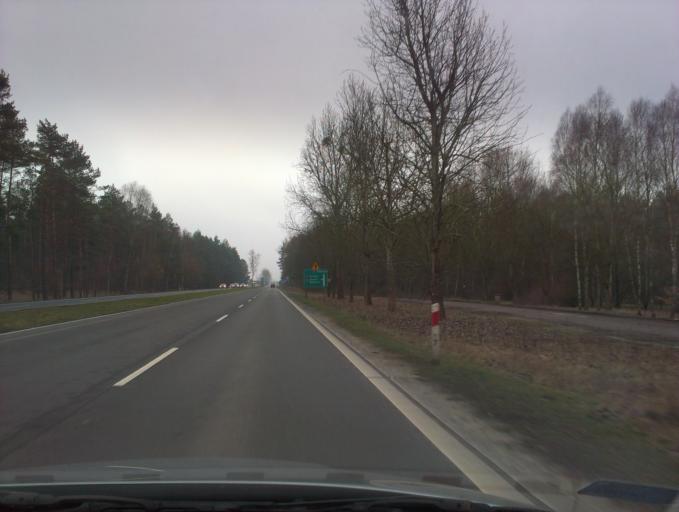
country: PL
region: Greater Poland Voivodeship
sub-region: Powiat pilski
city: Pila
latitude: 53.1159
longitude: 16.7515
